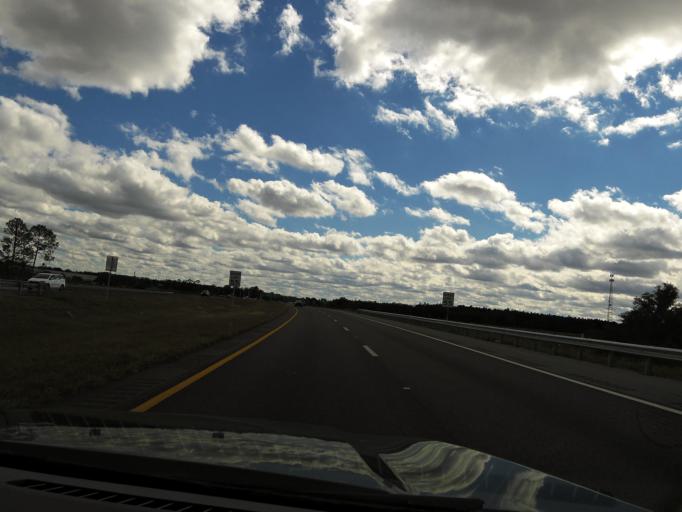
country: US
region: Florida
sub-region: Bradford County
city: Starke
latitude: 29.9222
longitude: -82.1379
